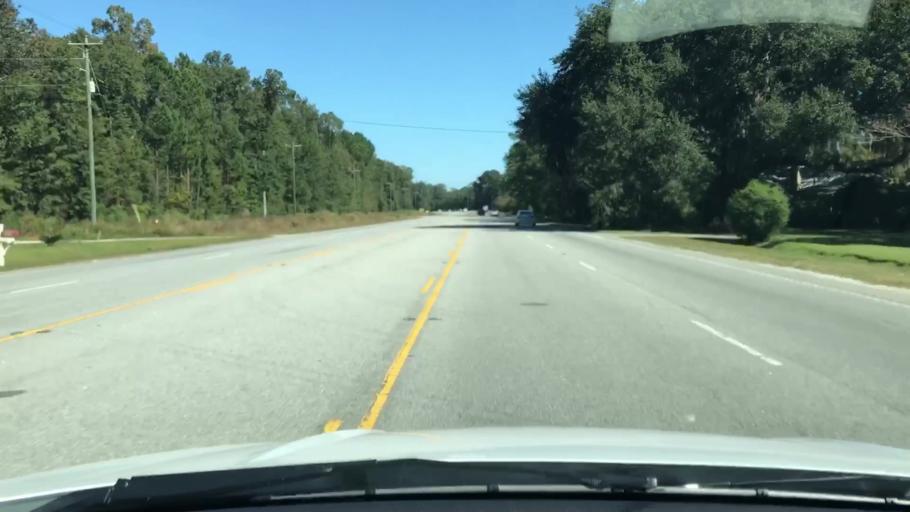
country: US
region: South Carolina
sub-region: Beaufort County
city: Bluffton
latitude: 32.3566
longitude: -80.8812
